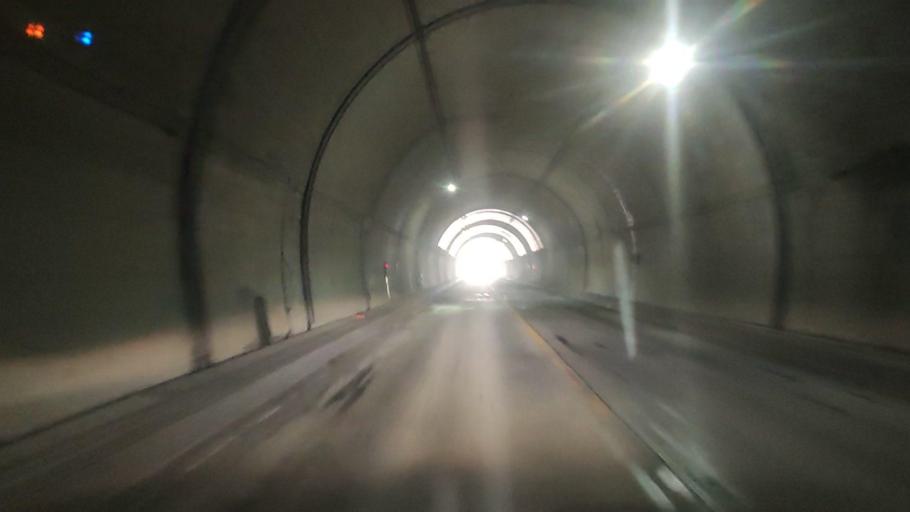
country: JP
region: Oita
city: Saiki
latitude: 32.8850
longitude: 131.9453
